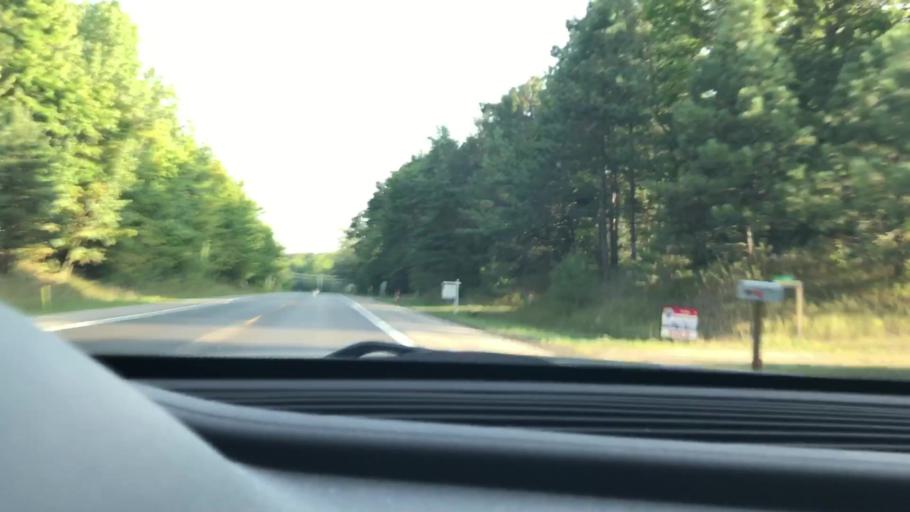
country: US
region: Michigan
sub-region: Antrim County
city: Bellaire
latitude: 45.0504
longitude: -85.3496
